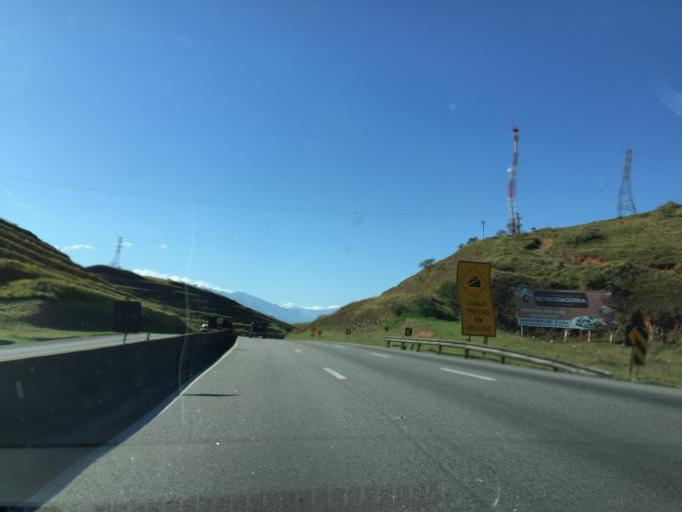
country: BR
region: Sao Paulo
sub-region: Cruzeiro
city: Cruzeiro
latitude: -22.6388
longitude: -44.9376
